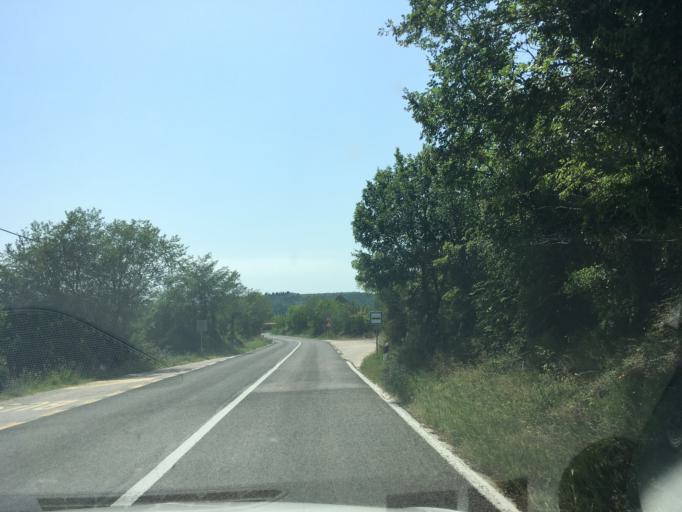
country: HR
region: Sibensko-Kniniska
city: Zaton
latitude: 43.9309
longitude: 15.8318
